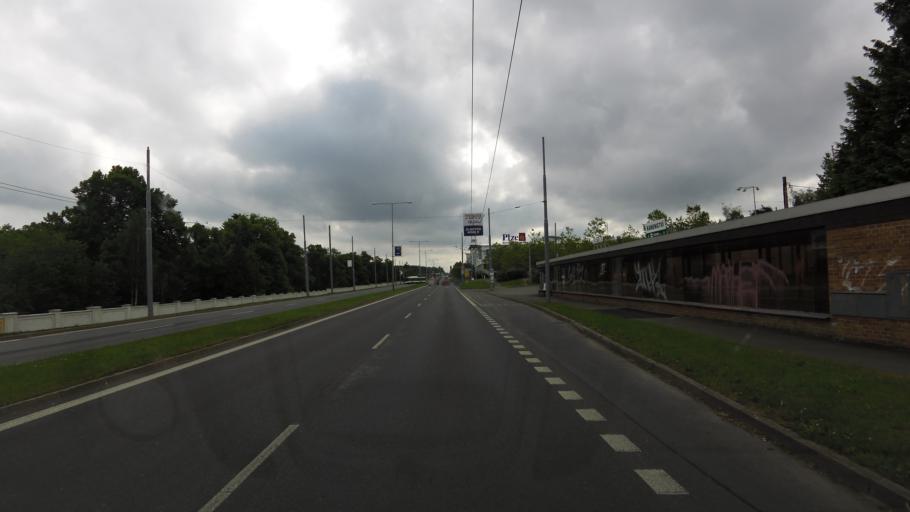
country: CZ
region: Plzensky
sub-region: Okres Plzen-Mesto
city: Pilsen
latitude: 49.7467
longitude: 13.4325
